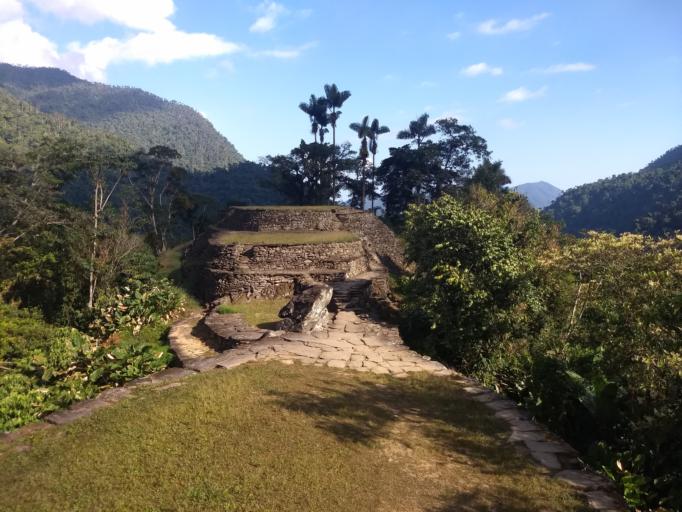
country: CO
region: Magdalena
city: Cienaga
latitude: 11.0376
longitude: -73.9252
